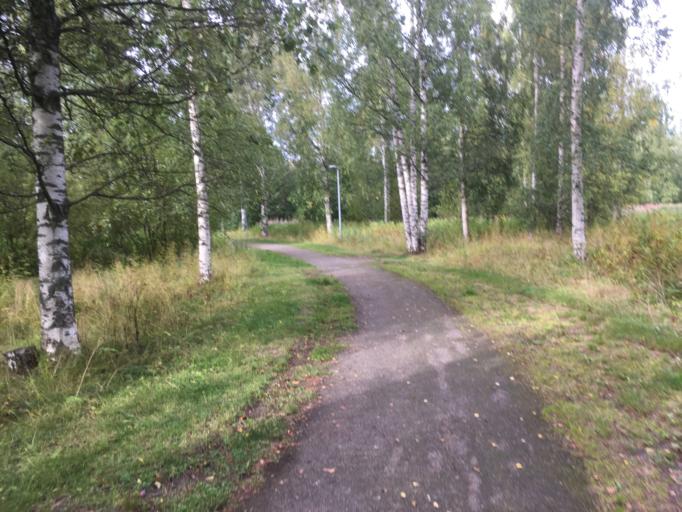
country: FI
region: Central Finland
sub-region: Jyvaeskylae
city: Jyvaeskylae
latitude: 62.2249
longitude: 25.7924
